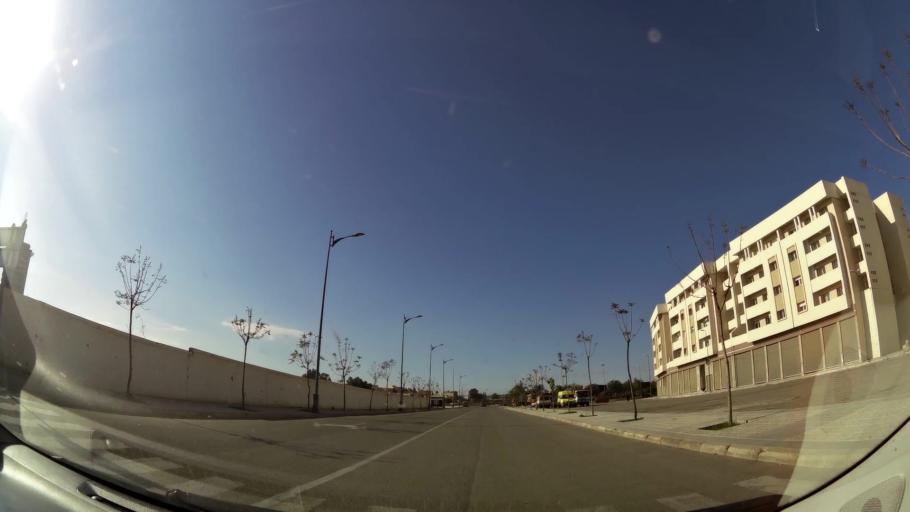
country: MA
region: Oriental
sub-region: Oujda-Angad
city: Oujda
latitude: 34.6787
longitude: -1.9276
